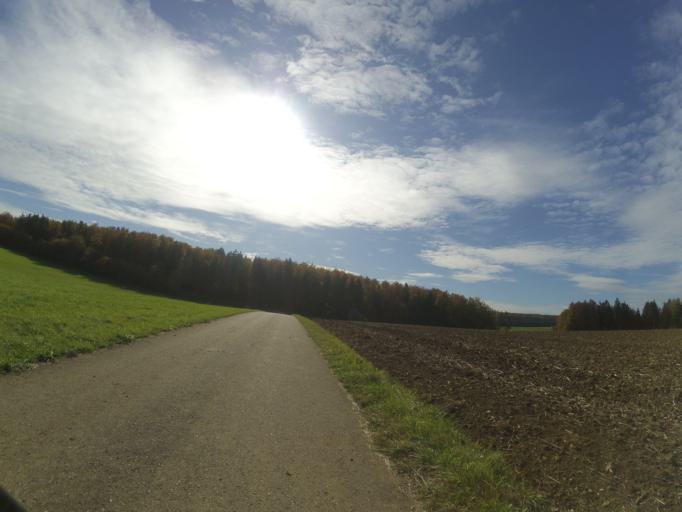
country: DE
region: Baden-Wuerttemberg
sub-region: Tuebingen Region
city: Lonsee
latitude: 48.5984
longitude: 9.9404
